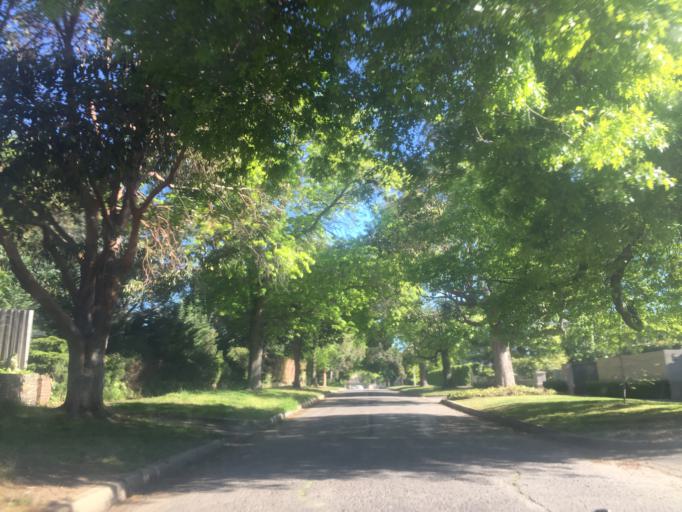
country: AU
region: Victoria
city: Balwyn
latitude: -37.8155
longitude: 145.0727
